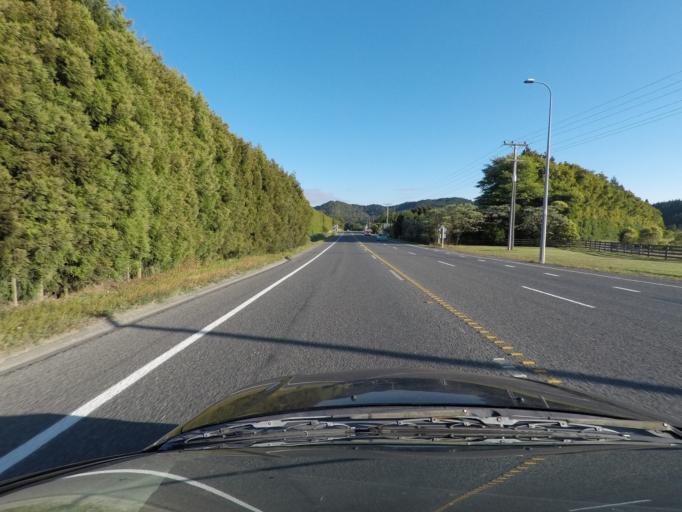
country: NZ
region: Northland
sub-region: Whangarei
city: Whangarei
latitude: -35.6333
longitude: 174.2961
